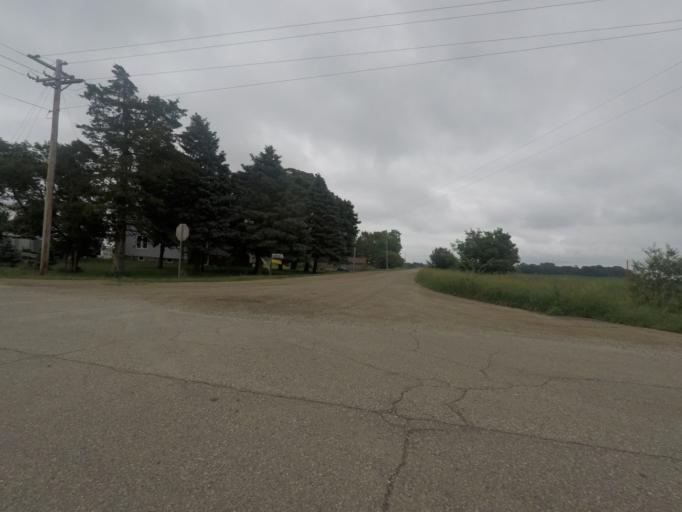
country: US
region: Minnesota
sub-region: Steele County
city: Owatonna
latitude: 44.0373
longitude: -93.0660
